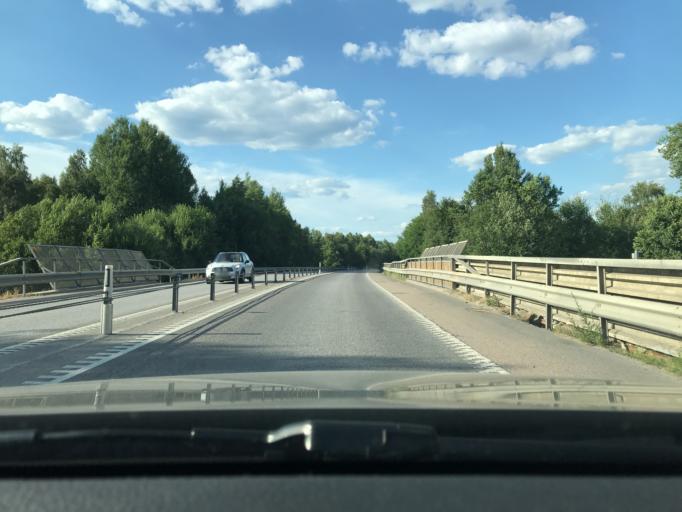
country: SE
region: Kronoberg
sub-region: Vaxjo Kommun
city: Vaexjoe
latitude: 56.8834
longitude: 14.7461
